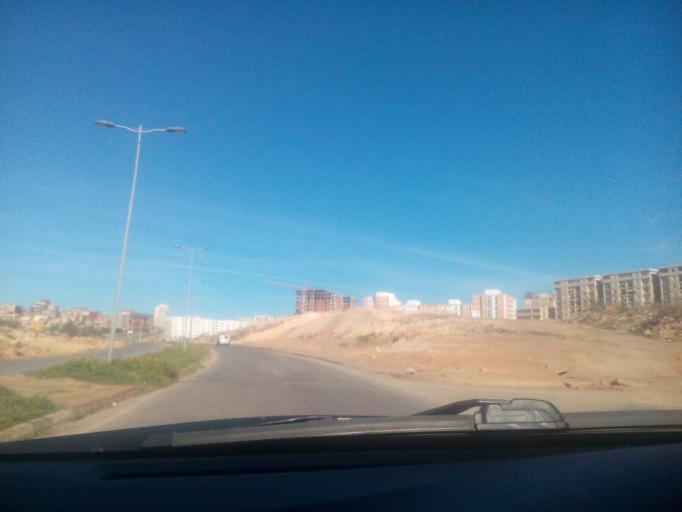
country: DZ
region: Oran
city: Bir el Djir
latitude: 35.7399
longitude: -0.5463
